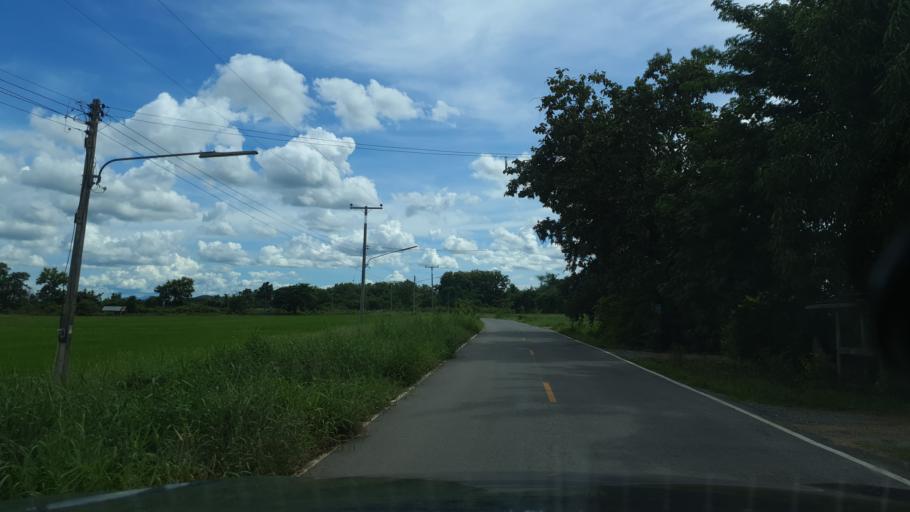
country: TH
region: Sukhothai
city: Thung Saliam
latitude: 17.3520
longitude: 99.6411
